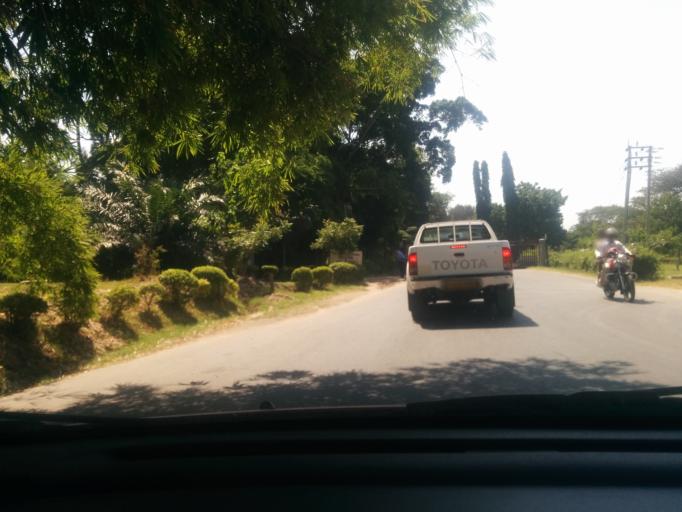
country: TZ
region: Dar es Salaam
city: Magomeni
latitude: -6.7680
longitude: 39.2142
